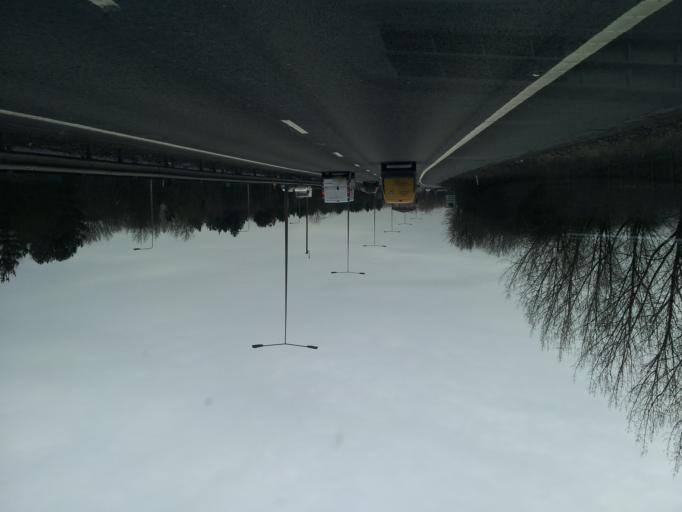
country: GB
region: England
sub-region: Cambridgeshire
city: Girton
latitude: 52.2371
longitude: 0.0637
